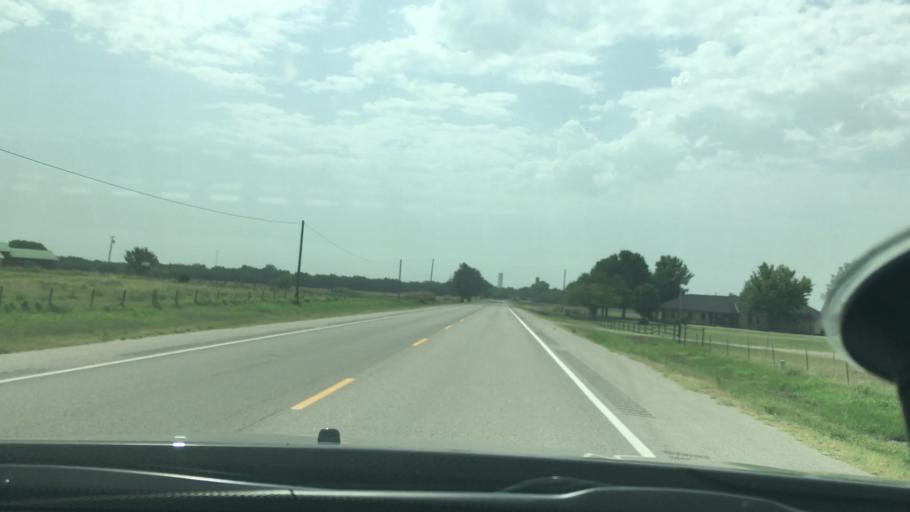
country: US
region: Oklahoma
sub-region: Garvin County
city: Pauls Valley
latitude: 34.8364
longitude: -97.2672
